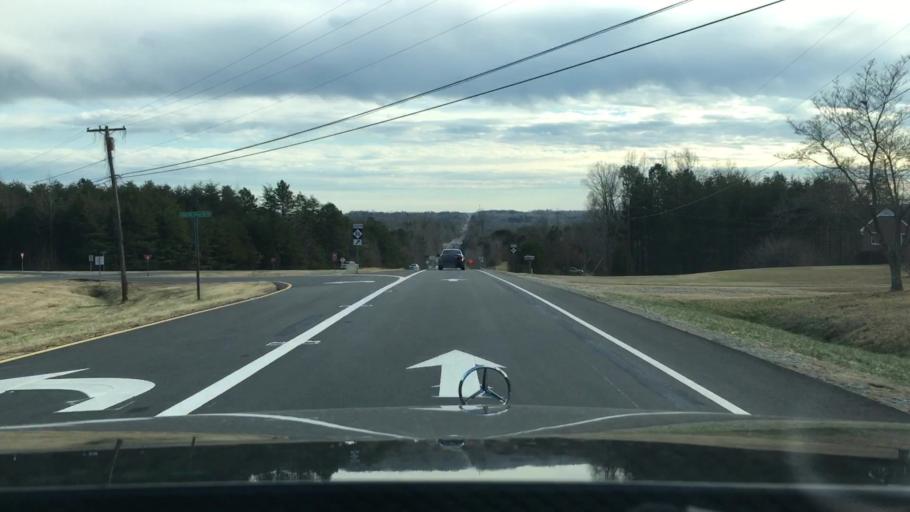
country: US
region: Virginia
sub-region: City of Danville
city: Danville
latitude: 36.5231
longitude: -79.3960
